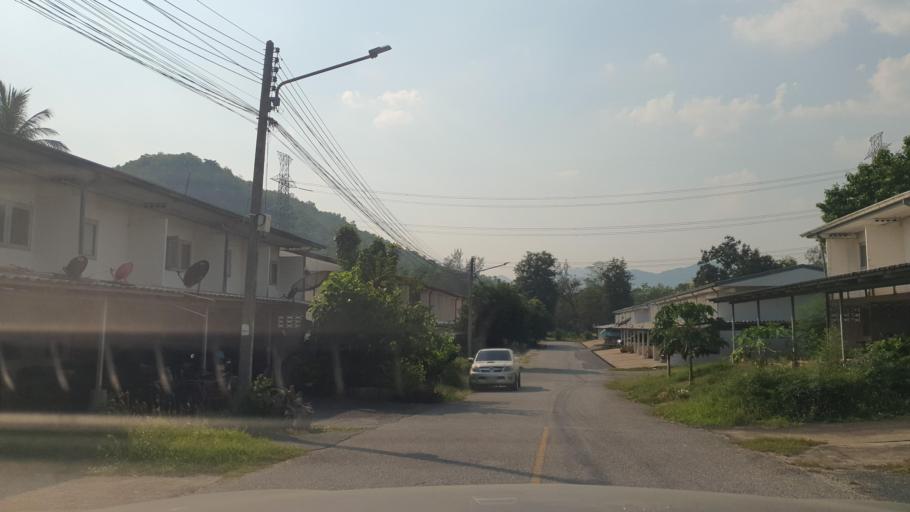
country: TH
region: Kanchanaburi
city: Sai Yok
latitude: 14.2262
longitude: 99.2337
